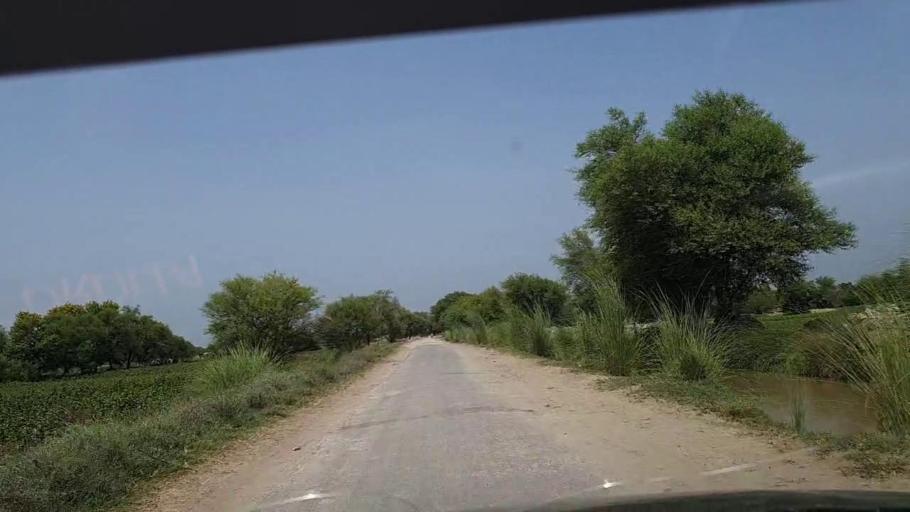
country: PK
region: Sindh
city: Khanpur
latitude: 27.8097
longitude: 69.4505
